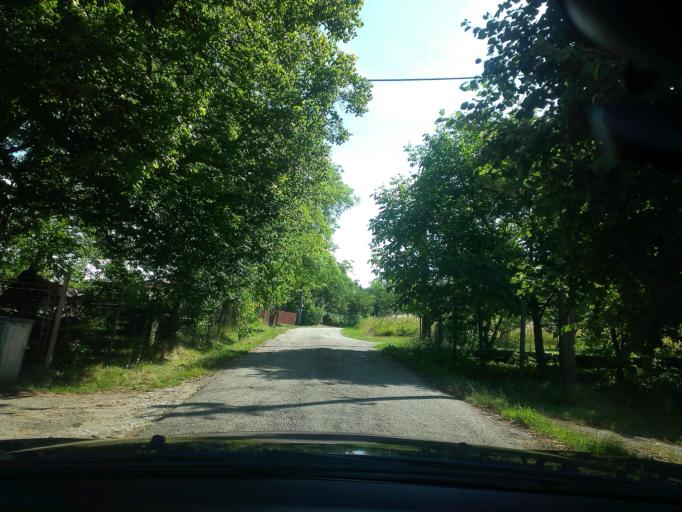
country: SK
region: Trenciansky
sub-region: Okres Myjava
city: Myjava
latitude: 48.7902
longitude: 17.5888
